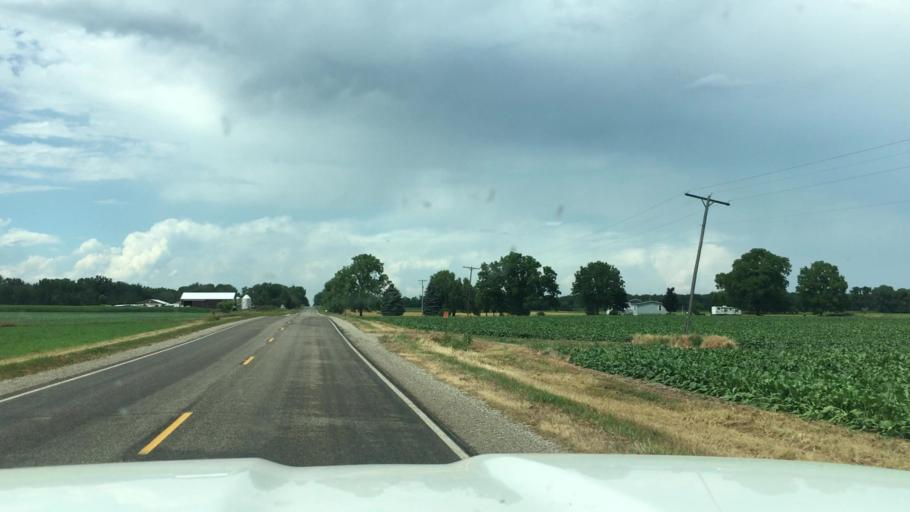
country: US
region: Michigan
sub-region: Montcalm County
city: Carson City
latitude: 43.2284
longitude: -84.7776
